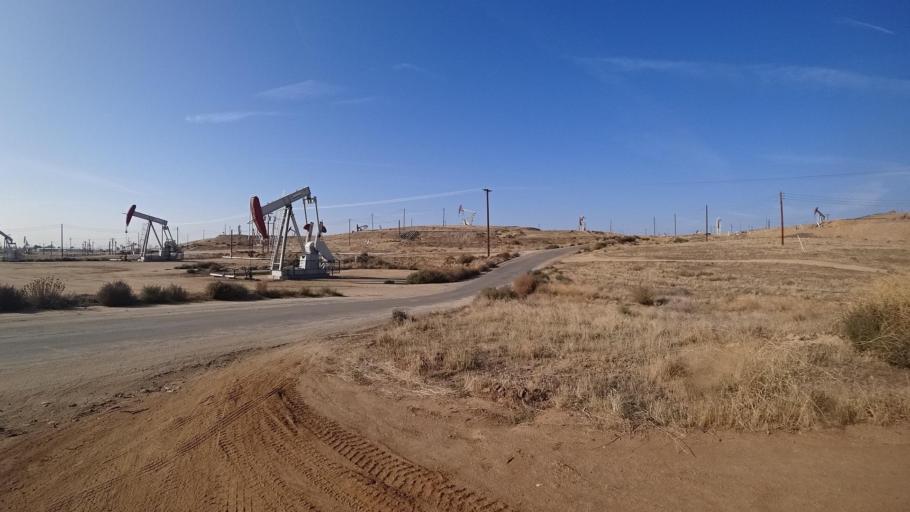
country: US
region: California
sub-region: Kern County
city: Oildale
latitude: 35.4670
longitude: -119.0266
